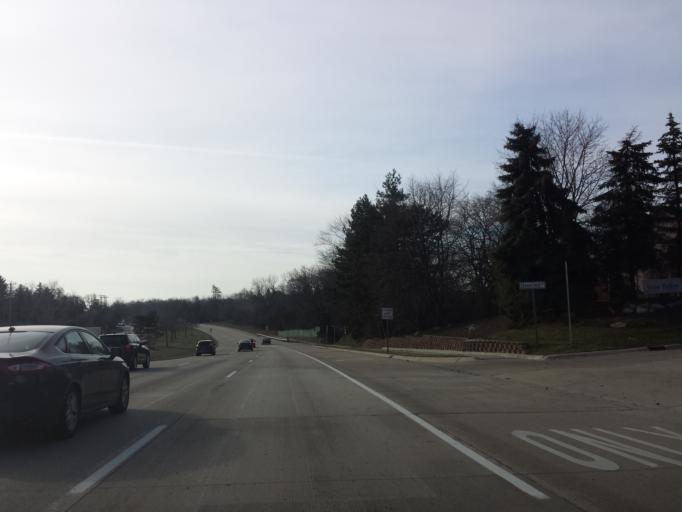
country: US
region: Michigan
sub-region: Oakland County
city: Bloomfield Hills
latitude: 42.5627
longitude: -83.2845
